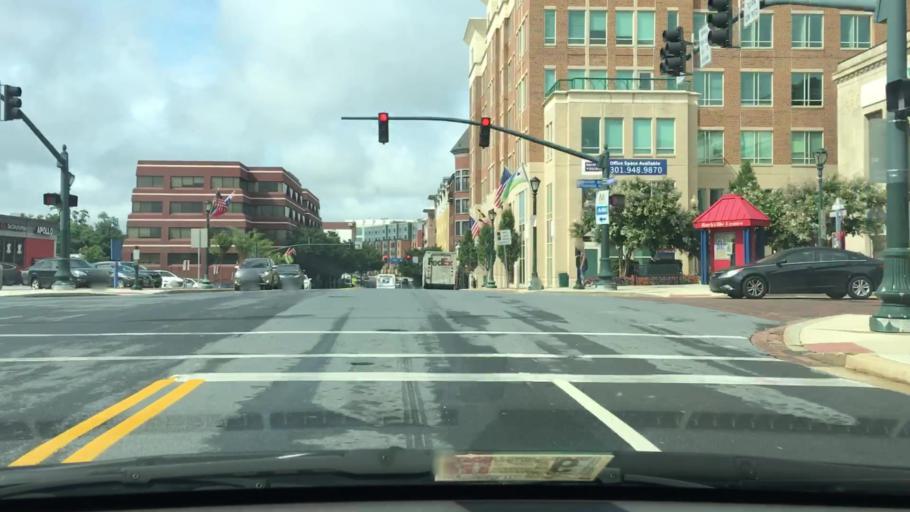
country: US
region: Maryland
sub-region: Montgomery County
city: Rockville
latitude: 39.0840
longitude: -77.1529
